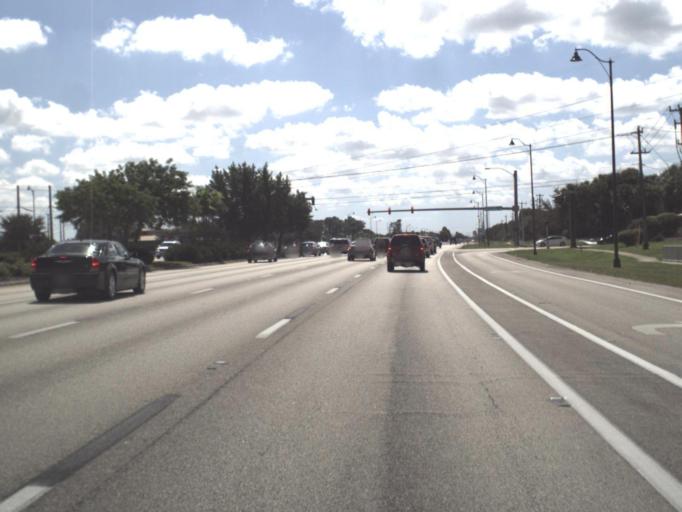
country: US
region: Florida
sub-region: Lee County
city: Bonita Springs
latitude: 26.3819
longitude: -81.8082
